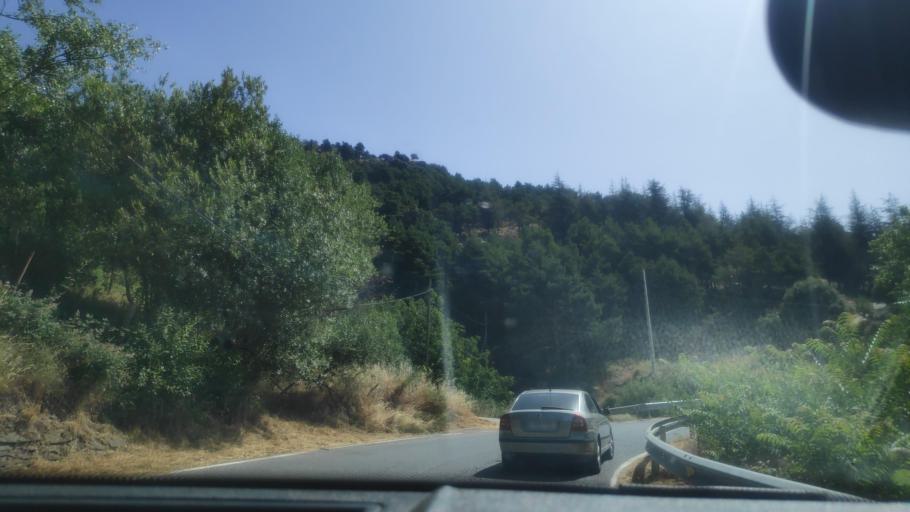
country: ES
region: Andalusia
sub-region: Provincia de Granada
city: Trevelez
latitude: 36.9839
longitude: -3.2776
